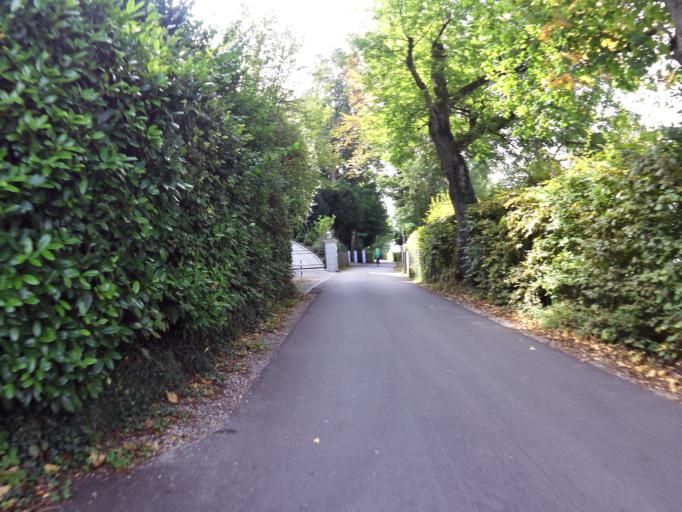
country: DE
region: Bavaria
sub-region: Upper Bavaria
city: Berg
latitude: 47.9482
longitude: 11.3417
